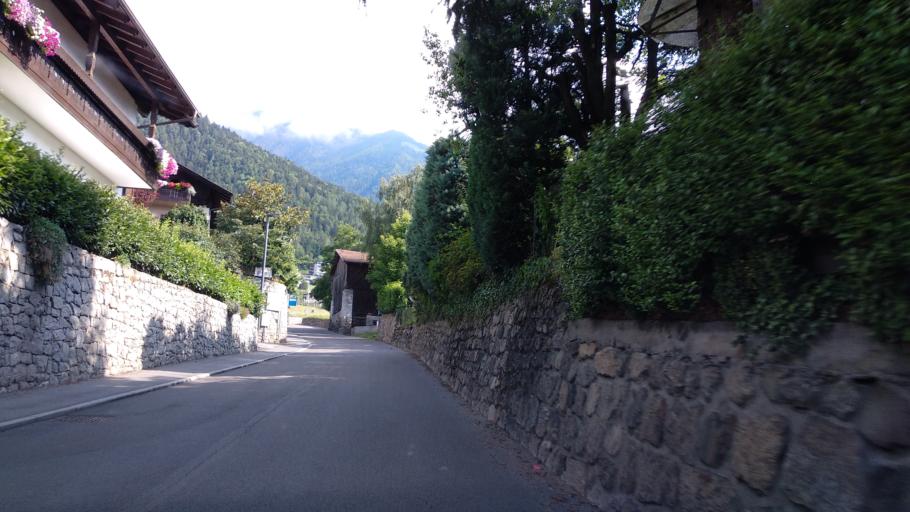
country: IT
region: Trentino-Alto Adige
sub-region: Bolzano
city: Tirolo
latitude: 46.6941
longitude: 11.1543
